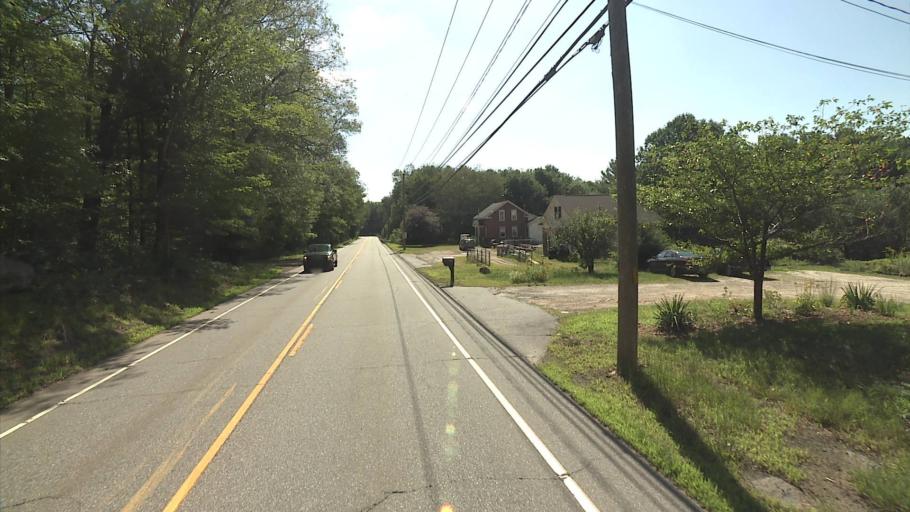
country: US
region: Connecticut
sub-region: Tolland County
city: Stafford
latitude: 41.9625
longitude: -72.2356
